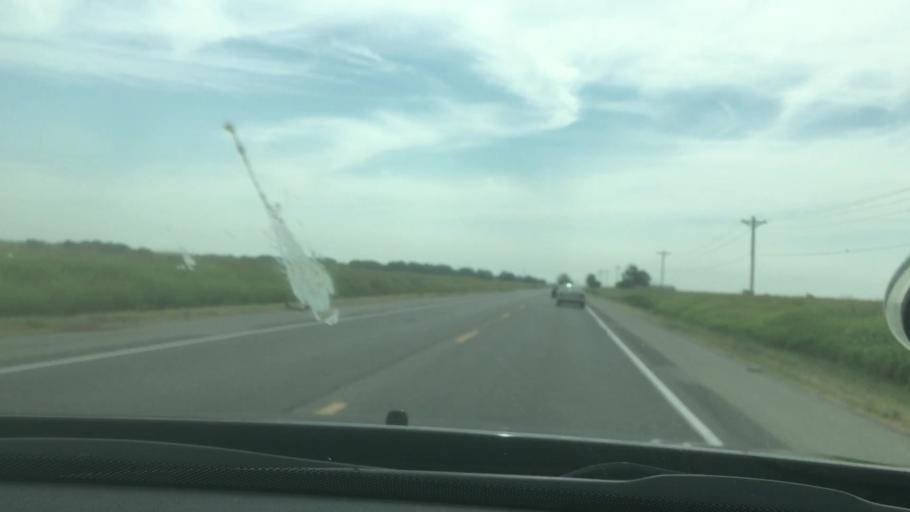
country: US
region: Oklahoma
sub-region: Garvin County
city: Lindsay
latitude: 34.8251
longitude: -97.5428
